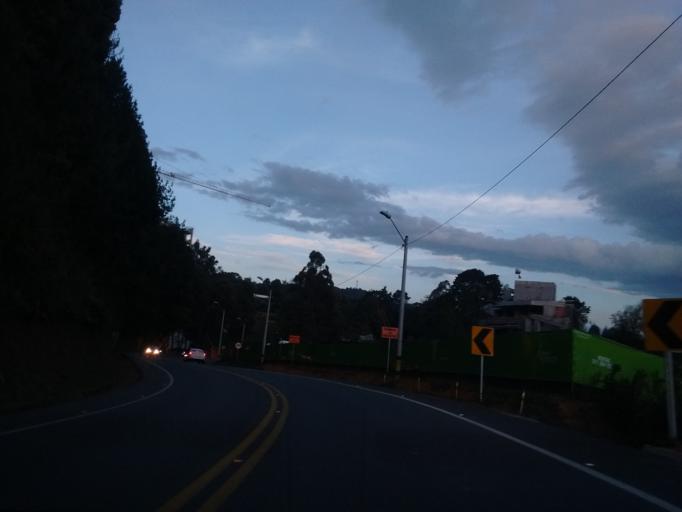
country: CO
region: Antioquia
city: Envigado
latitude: 6.1560
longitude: -75.5327
